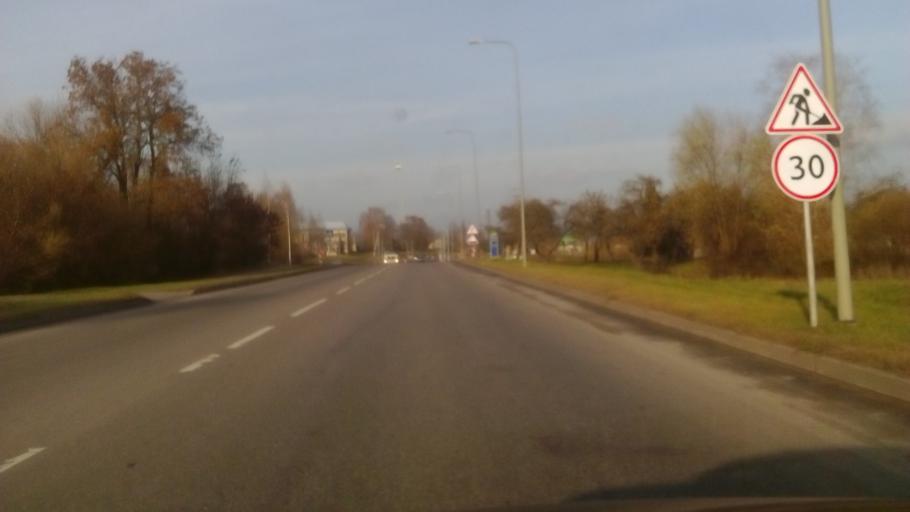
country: LT
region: Alytaus apskritis
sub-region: Alytus
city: Alytus
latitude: 54.4066
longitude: 24.0036
